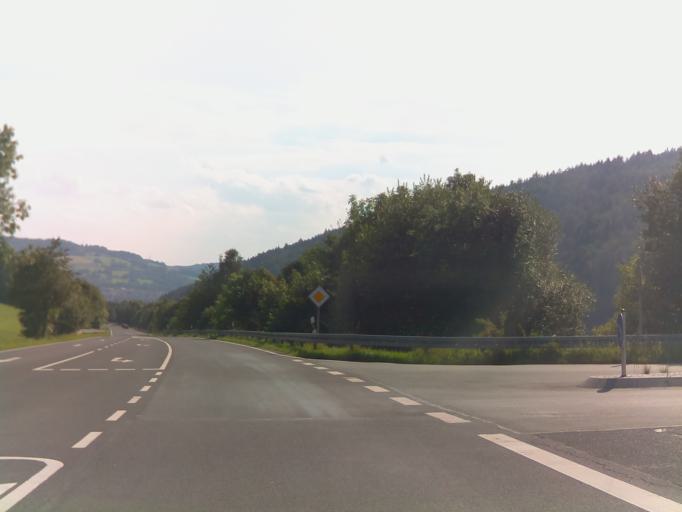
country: DE
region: Bavaria
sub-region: Regierungsbezirk Unterfranken
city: Riedenberg
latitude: 50.3449
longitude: 9.8832
